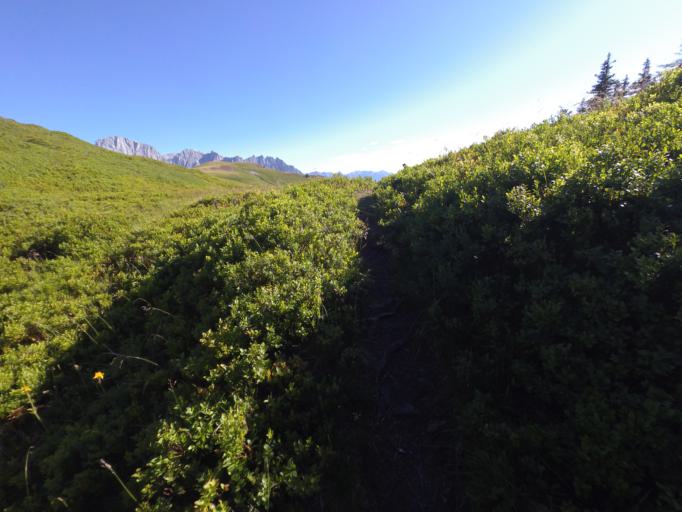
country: AT
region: Salzburg
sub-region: Politischer Bezirk Sankt Johann im Pongau
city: Goldegg
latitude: 47.3625
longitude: 13.0699
